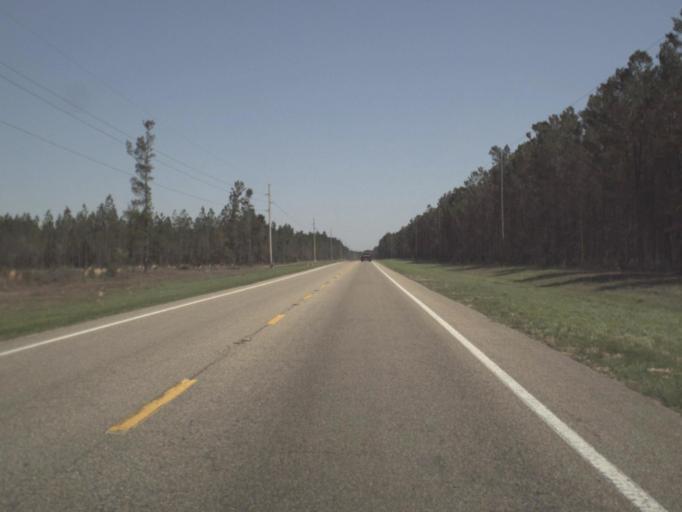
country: US
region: Florida
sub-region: Liberty County
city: Bristol
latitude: 30.4200
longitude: -84.8950
